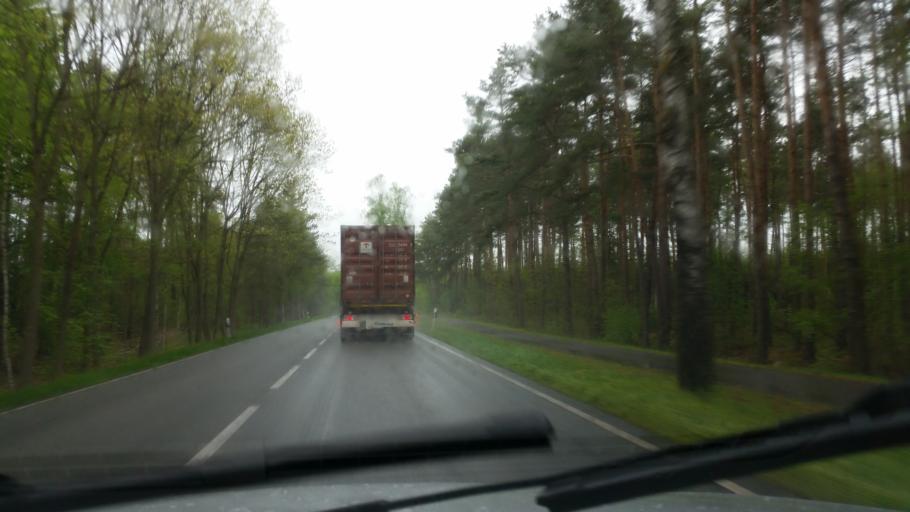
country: DE
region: Saxony-Anhalt
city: Kalbe
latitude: 52.6384
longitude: 11.3045
